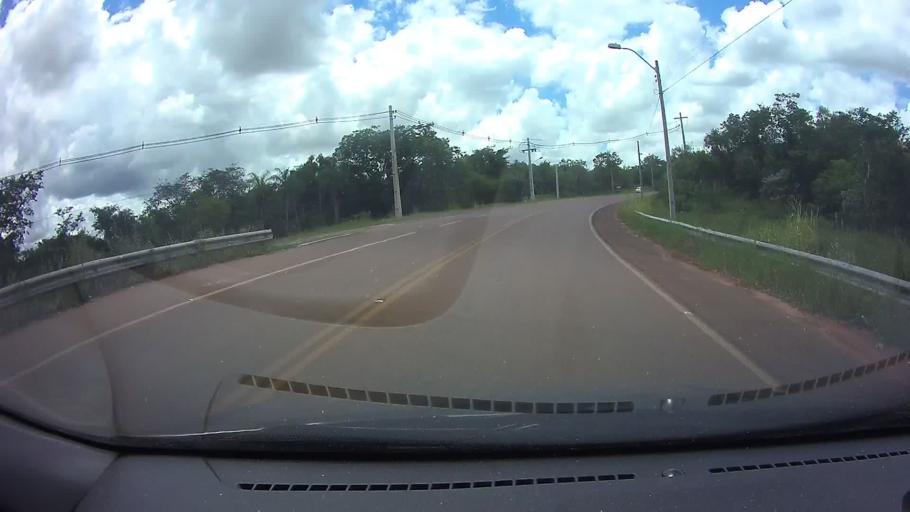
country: PY
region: Paraguari
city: La Colmena
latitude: -25.8919
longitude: -56.8308
